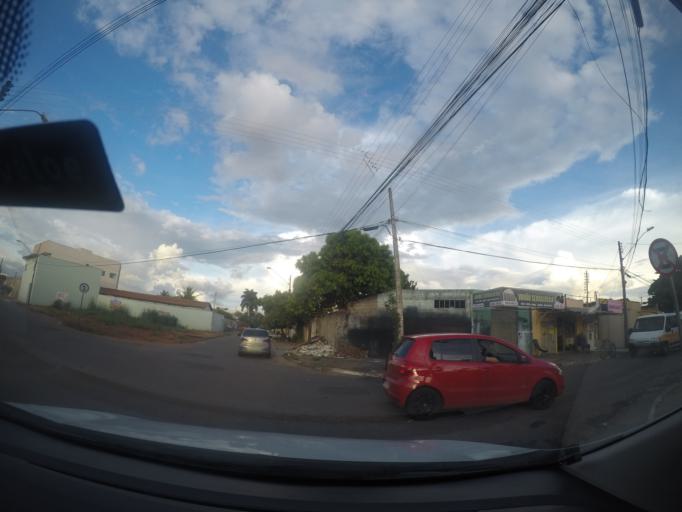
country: BR
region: Goias
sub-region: Goiania
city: Goiania
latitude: -16.6880
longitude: -49.3169
